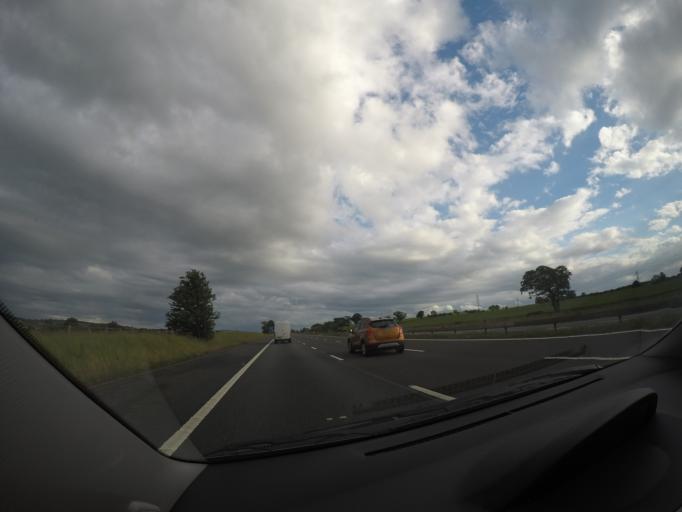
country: GB
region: England
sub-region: Cumbria
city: Penrith
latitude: 54.7072
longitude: -2.7926
